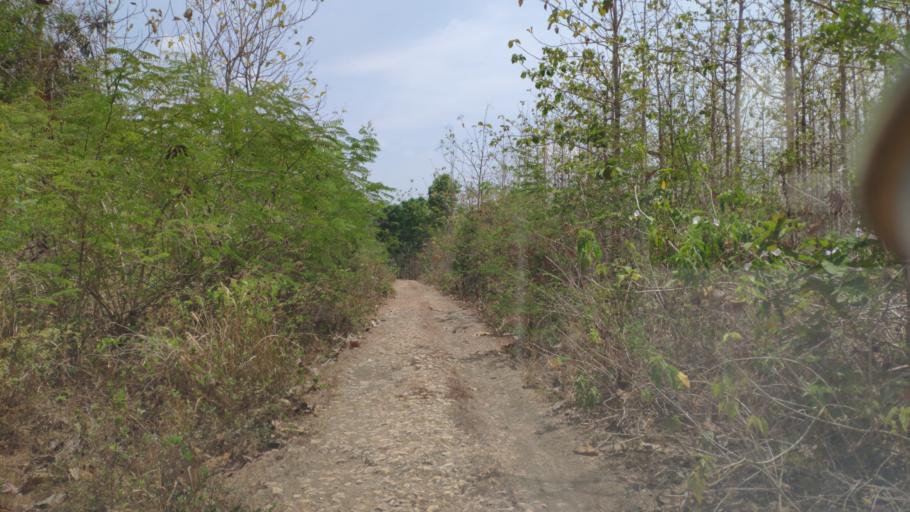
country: ID
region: Central Java
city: Padaan
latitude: -6.9332
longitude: 111.3042
